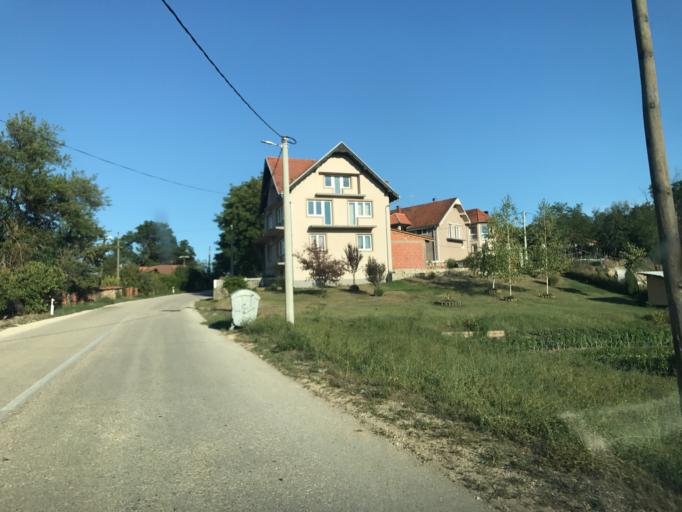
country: RO
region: Mehedinti
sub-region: Comuna Gogosu
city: Ostrovu Mare
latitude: 44.2896
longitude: 22.3577
